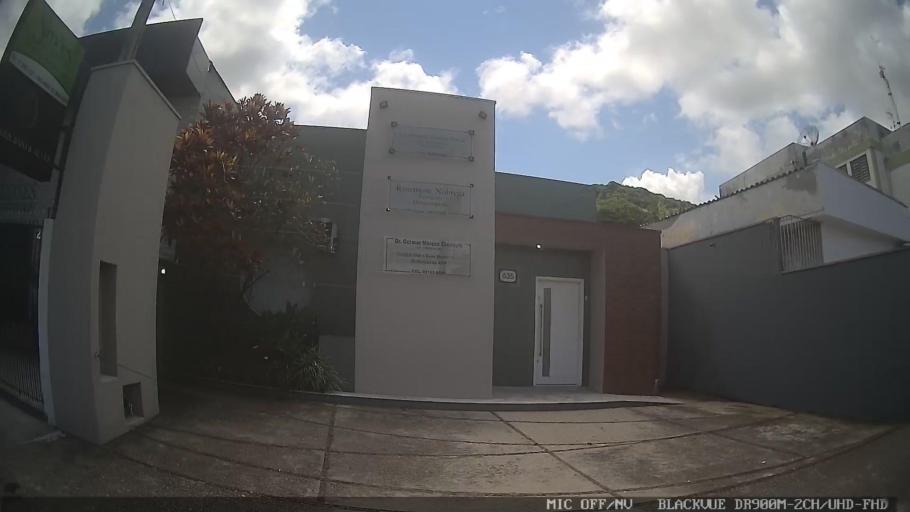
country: BR
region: Sao Paulo
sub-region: Caraguatatuba
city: Caraguatatuba
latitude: -23.6198
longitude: -45.4117
